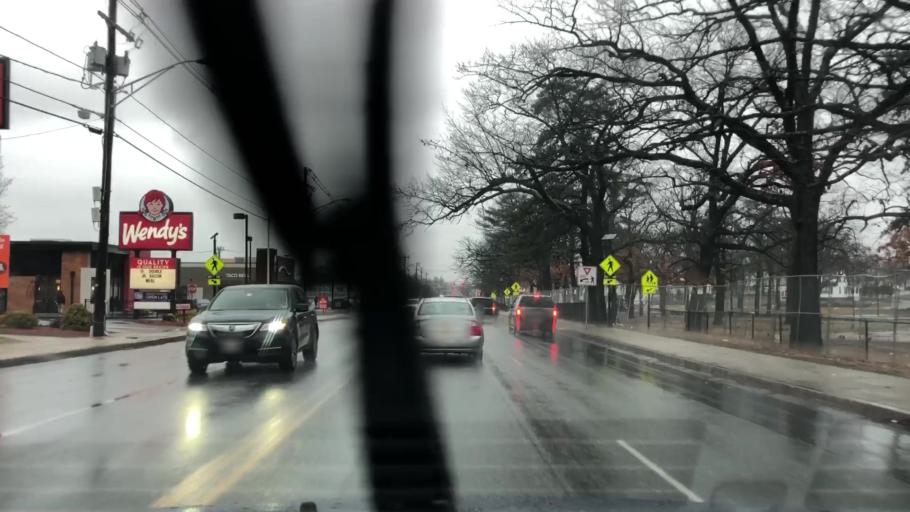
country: US
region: Massachusetts
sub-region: Essex County
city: North Andover
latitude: 42.6890
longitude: -71.1479
